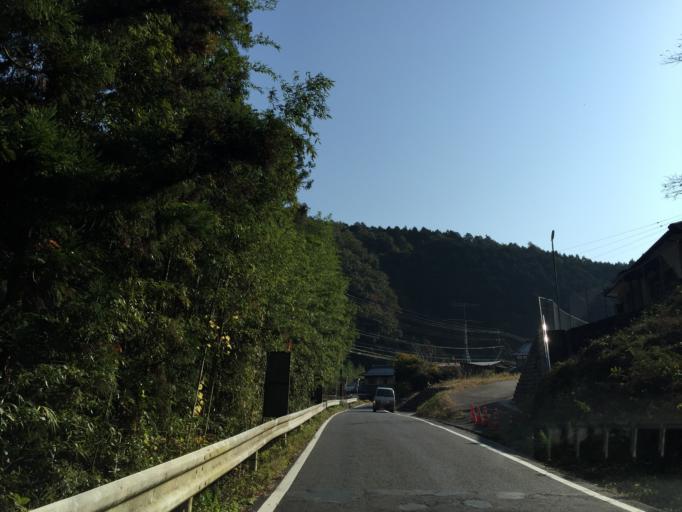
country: JP
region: Gifu
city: Minokamo
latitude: 35.5509
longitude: 137.1181
